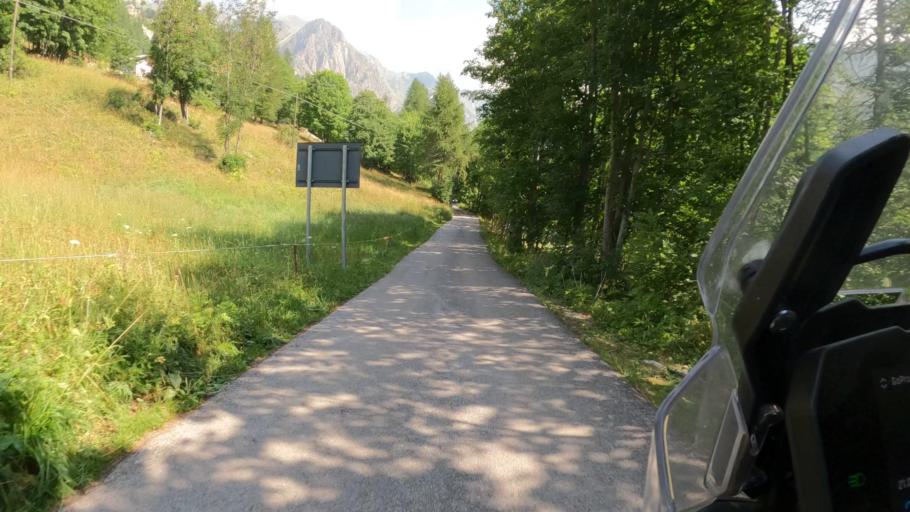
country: IT
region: Piedmont
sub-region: Provincia di Cuneo
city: Canosio
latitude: 44.4242
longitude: 7.0513
